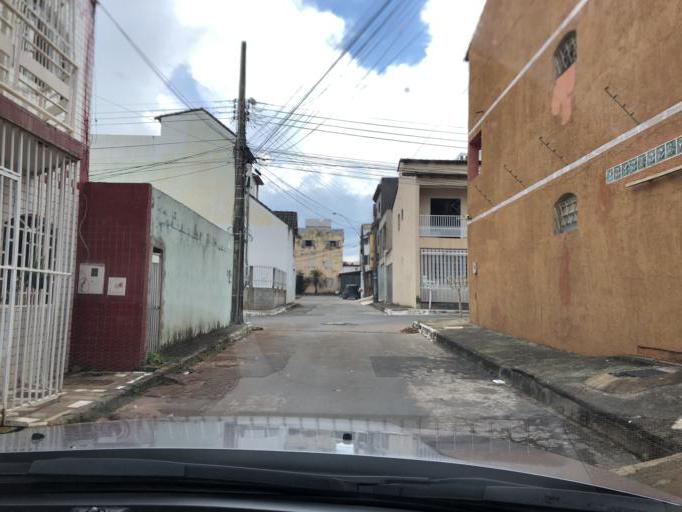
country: BR
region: Federal District
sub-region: Brasilia
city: Brasilia
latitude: -15.8542
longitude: -48.0331
